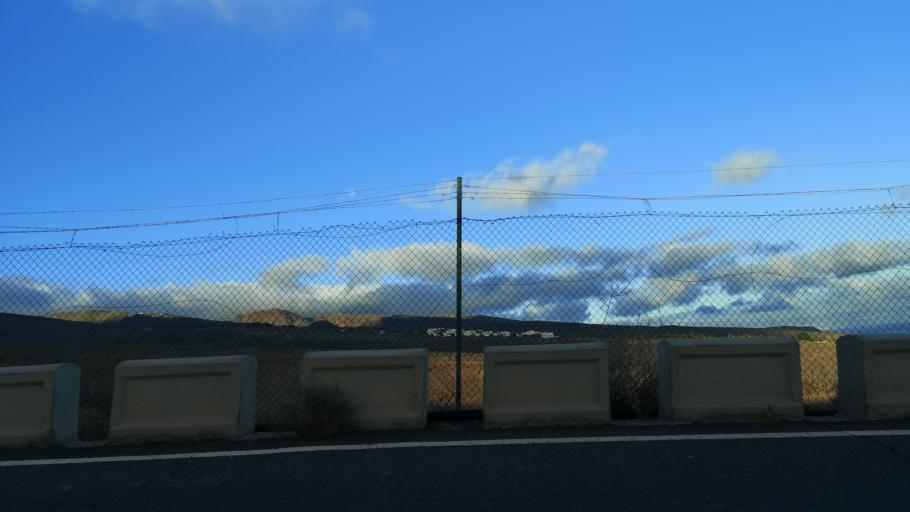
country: ES
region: Canary Islands
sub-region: Provincia de Santa Cruz de Tenerife
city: Alajero
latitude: 28.0316
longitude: -17.2061
